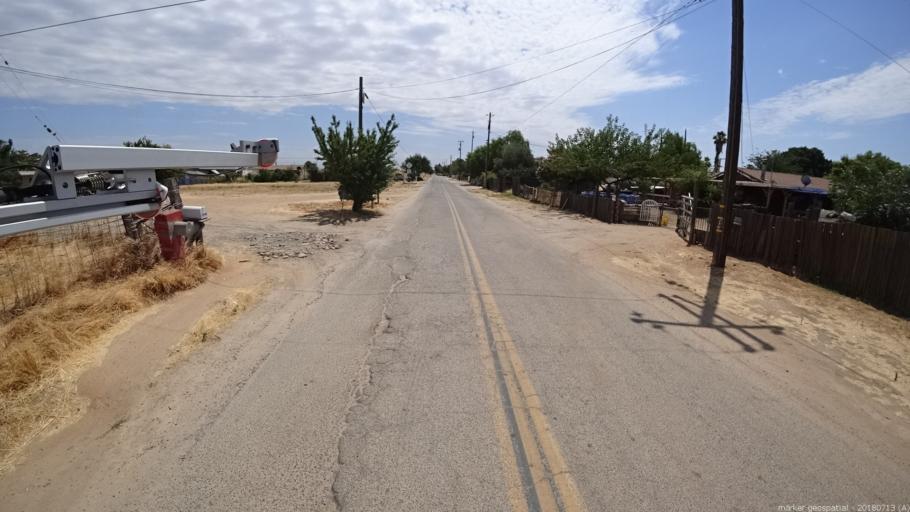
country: US
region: California
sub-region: Madera County
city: Madera Acres
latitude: 36.9926
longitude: -120.0597
